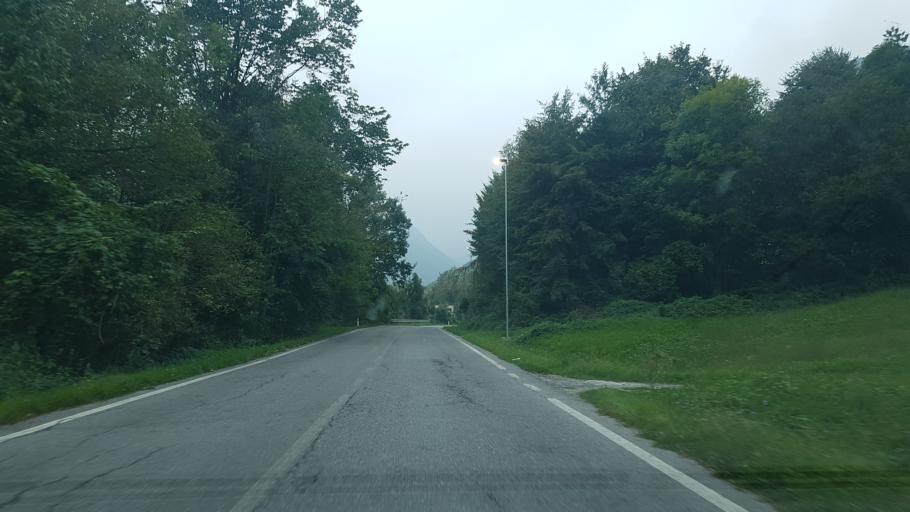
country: IT
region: Piedmont
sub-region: Provincia di Cuneo
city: Roccaforte Mondovi
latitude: 44.2771
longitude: 7.7420
